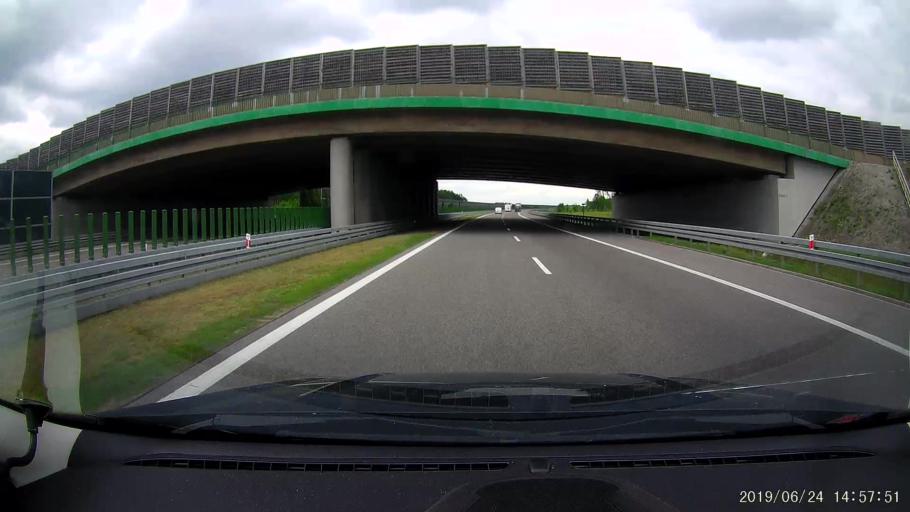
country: PL
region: Subcarpathian Voivodeship
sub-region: Powiat rzeszowski
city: Trzciana
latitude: 50.1182
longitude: 21.7959
